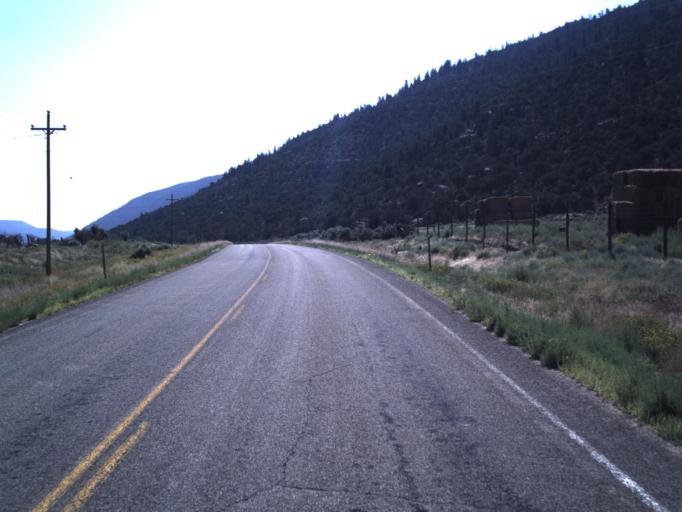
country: US
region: Utah
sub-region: Duchesne County
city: Duchesne
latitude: 40.2966
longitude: -110.5972
